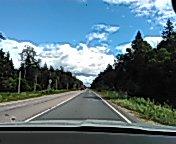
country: RU
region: Moskovskaya
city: Shevlyakovo
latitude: 56.5087
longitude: 36.7858
